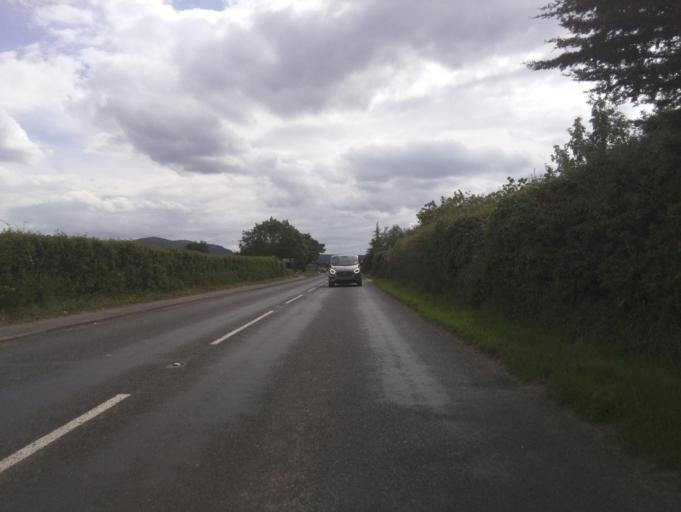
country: GB
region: England
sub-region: Worcestershire
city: Leigh
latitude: 52.1585
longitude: -2.3144
